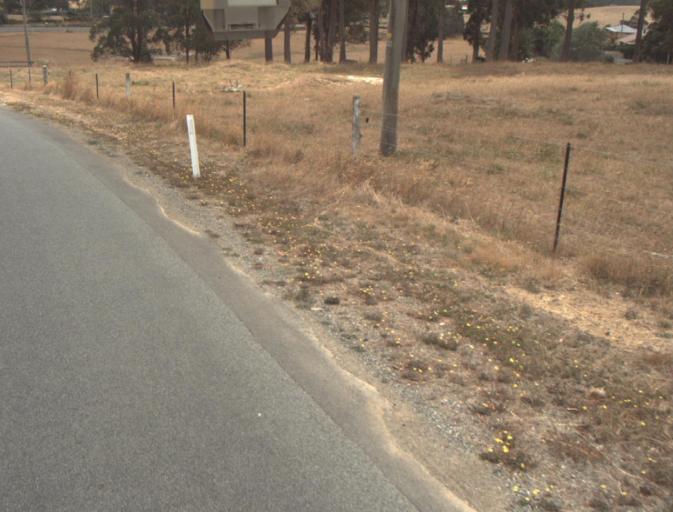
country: AU
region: Tasmania
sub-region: Launceston
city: Mayfield
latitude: -41.2018
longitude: 147.2182
